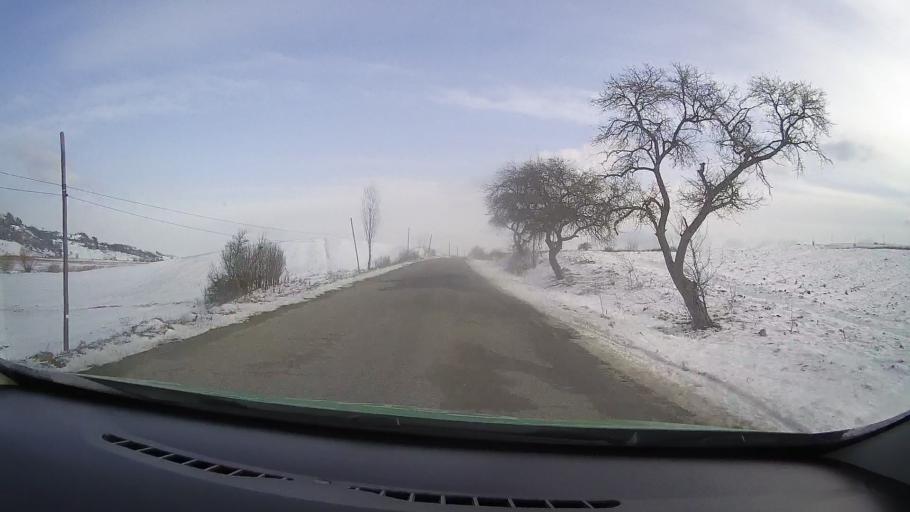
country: RO
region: Sibiu
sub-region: Comuna Merghindeal
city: Merghindeal
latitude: 45.9708
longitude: 24.7085
